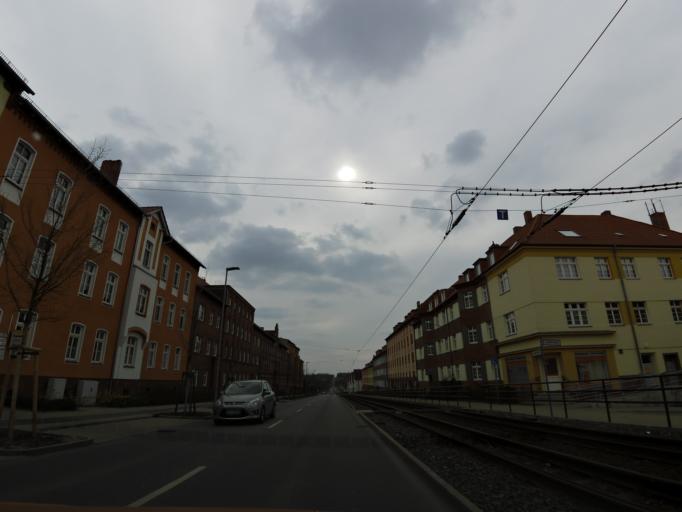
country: DE
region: Brandenburg
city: Frankfurt (Oder)
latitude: 52.3316
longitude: 14.5277
